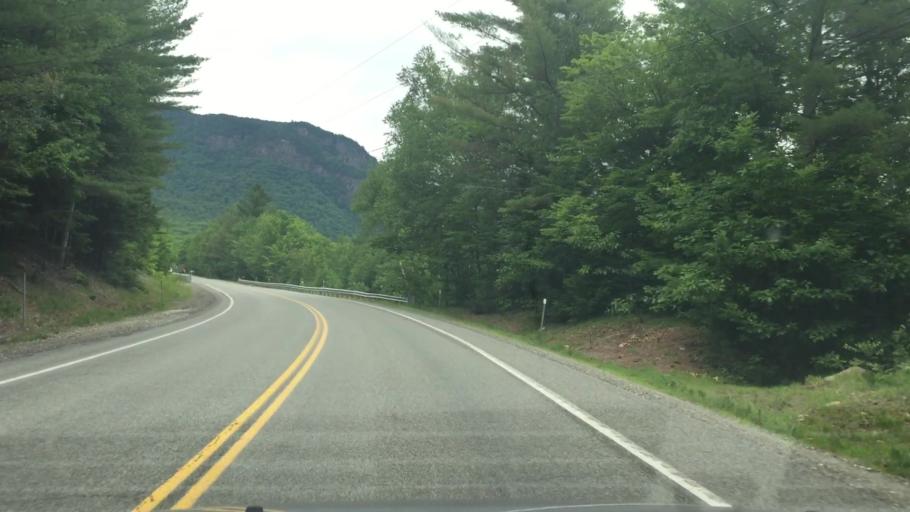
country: US
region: New Hampshire
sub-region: Carroll County
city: North Conway
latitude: 44.1353
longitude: -71.3601
